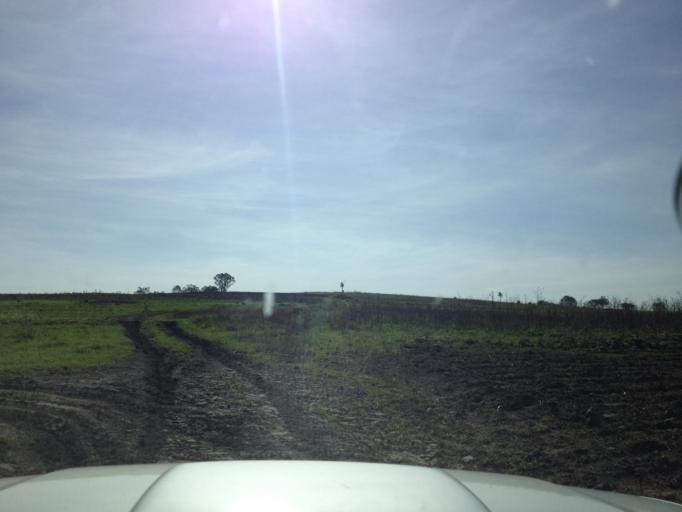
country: MX
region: Michoacan
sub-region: Tarimbaro
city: Pena del Panal
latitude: 19.7684
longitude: -101.1867
